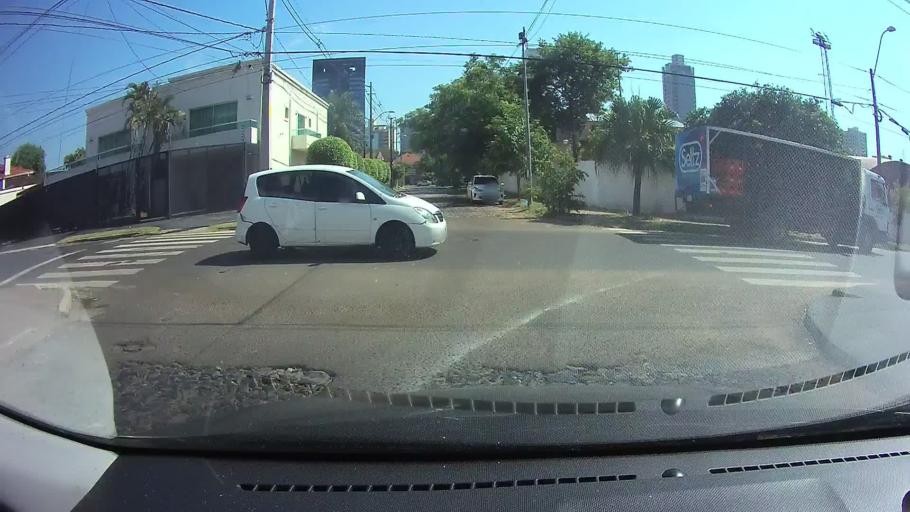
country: PY
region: Central
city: Fernando de la Mora
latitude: -25.2888
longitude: -57.5631
